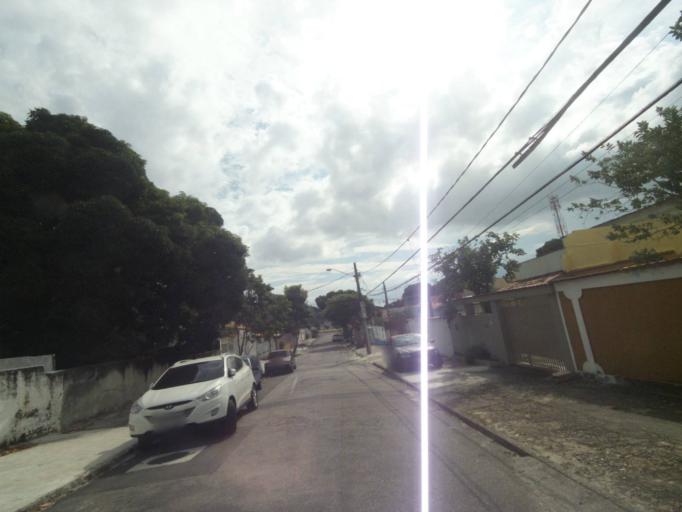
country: BR
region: Rio de Janeiro
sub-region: Nilopolis
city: Nilopolis
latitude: -22.8889
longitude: -43.3906
